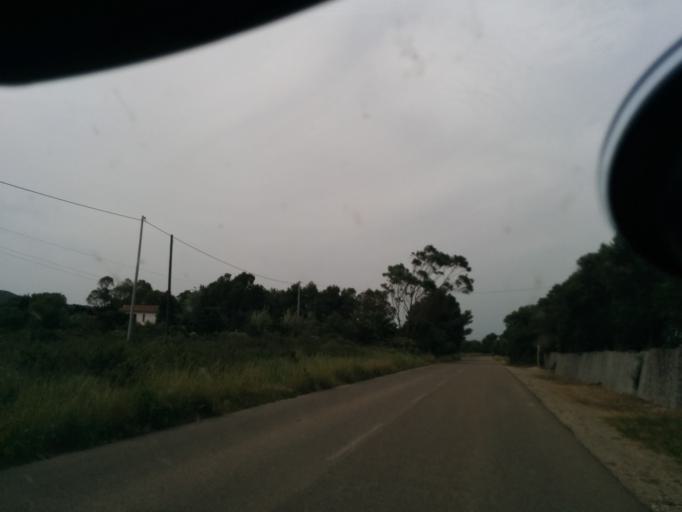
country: IT
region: Sardinia
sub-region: Provincia di Carbonia-Iglesias
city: Sant'Antioco
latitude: 39.0297
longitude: 8.4513
